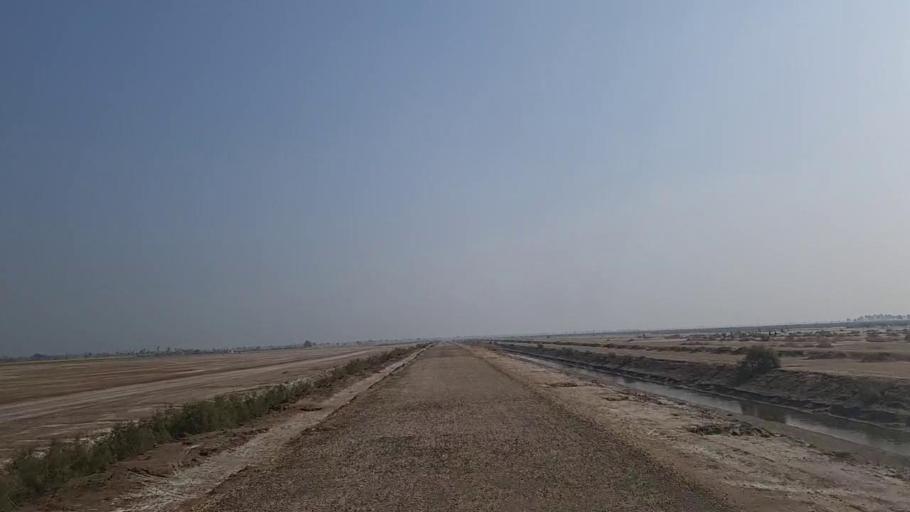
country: PK
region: Sindh
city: Nawabshah
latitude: 26.3461
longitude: 68.4463
